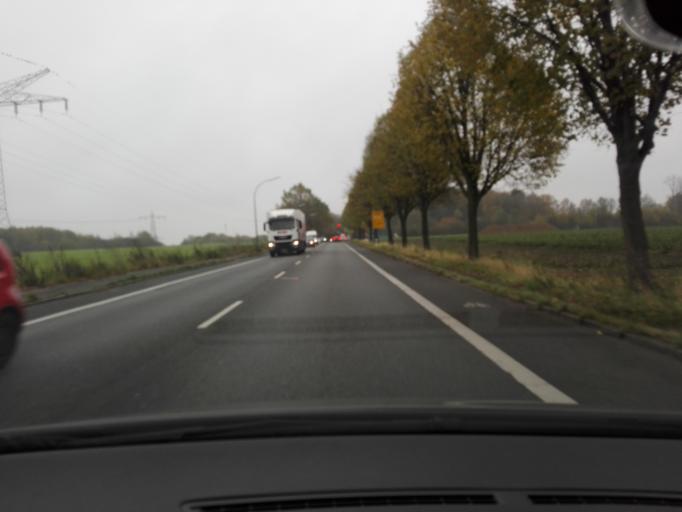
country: DE
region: North Rhine-Westphalia
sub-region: Regierungsbezirk Arnsberg
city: Holzwickede
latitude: 51.5096
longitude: 7.5743
